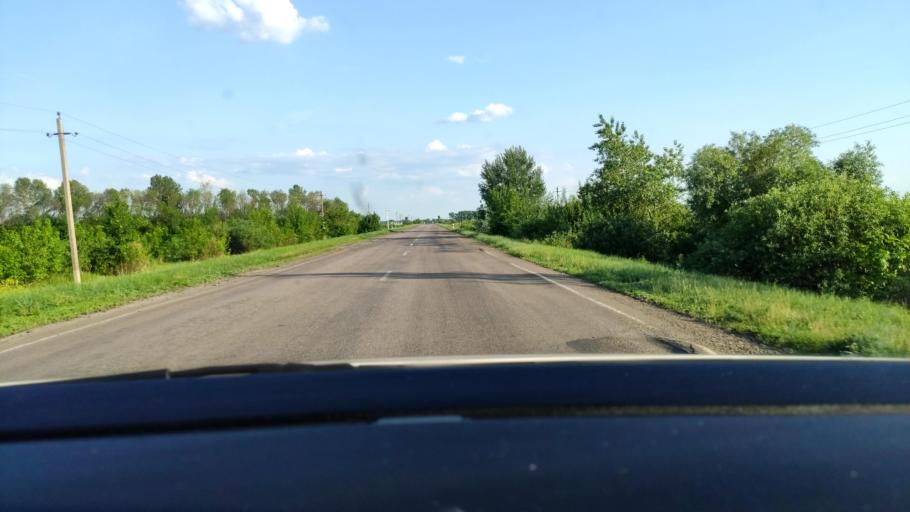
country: RU
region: Voronezj
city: Kashirskoye
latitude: 51.4805
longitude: 39.8576
